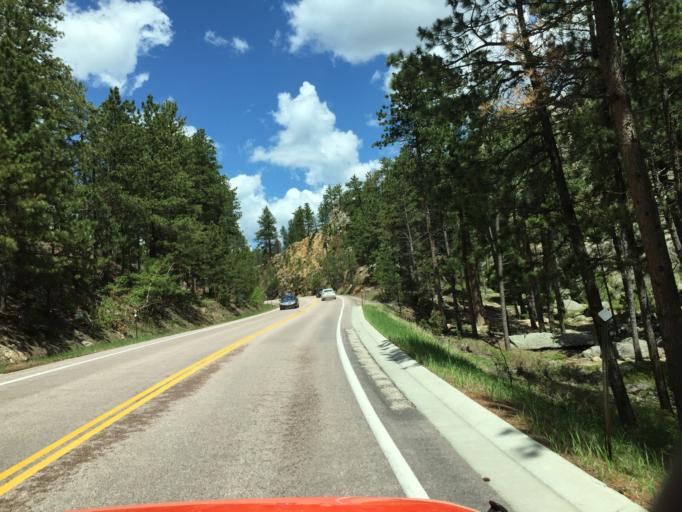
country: US
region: South Dakota
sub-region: Custer County
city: Custer
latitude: 43.8825
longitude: -103.4634
